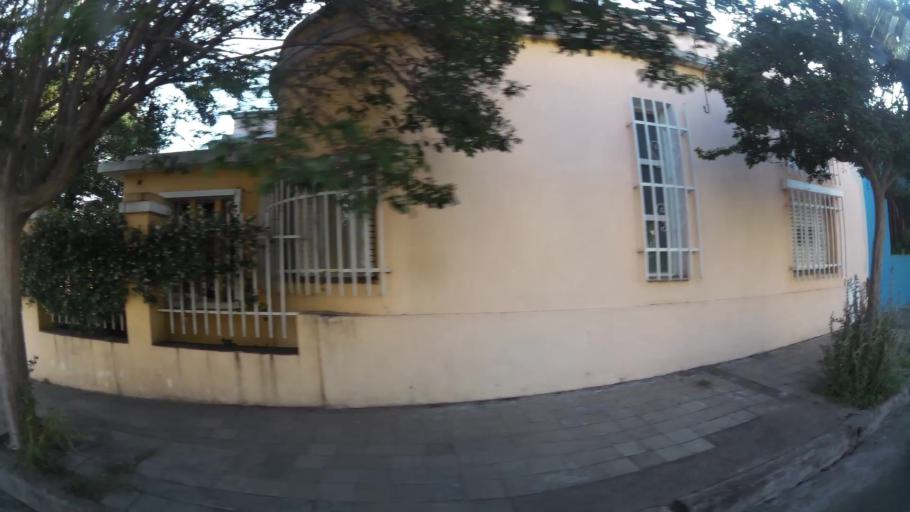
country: AR
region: Cordoba
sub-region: Departamento de Capital
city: Cordoba
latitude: -31.3848
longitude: -64.2223
